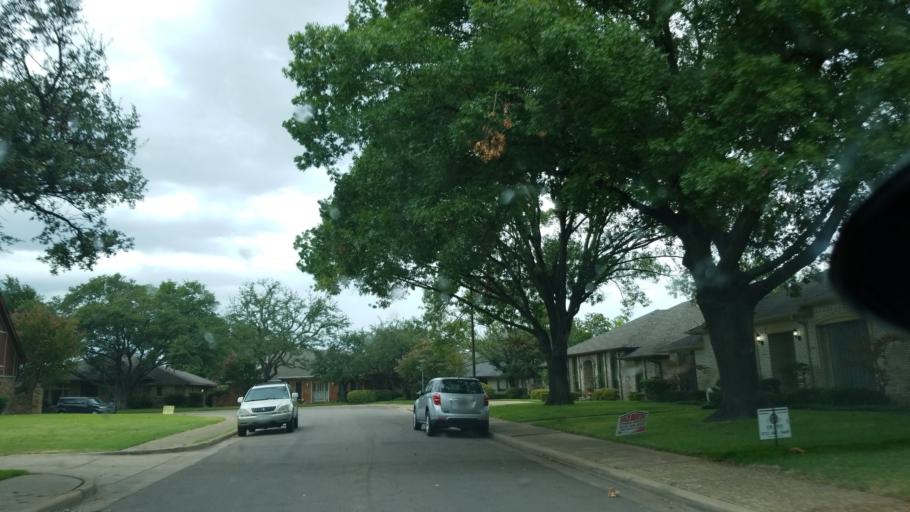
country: US
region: Texas
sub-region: Dallas County
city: Richardson
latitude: 32.8962
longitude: -96.7352
